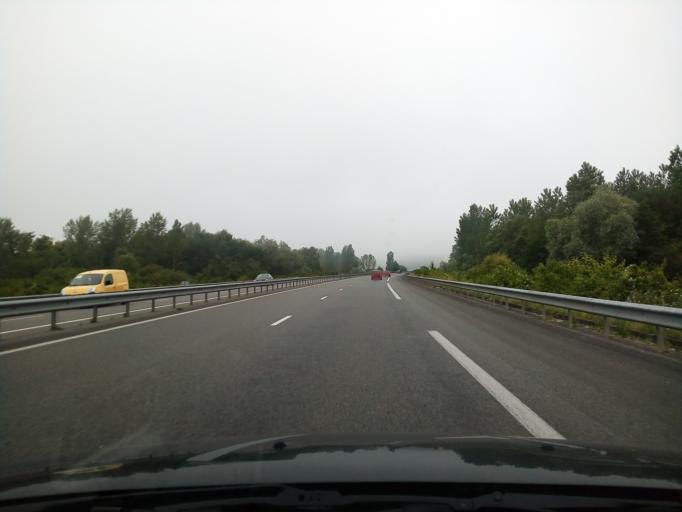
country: FR
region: Poitou-Charentes
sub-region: Departement de la Charente
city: Jarnac
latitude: 45.6695
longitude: -0.1652
